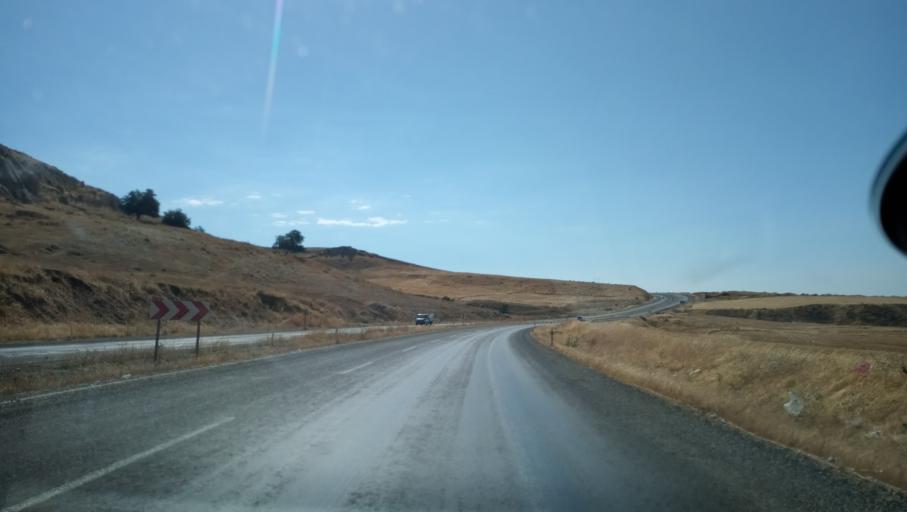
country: TR
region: Diyarbakir
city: Silvan
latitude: 38.1322
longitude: 41.0491
